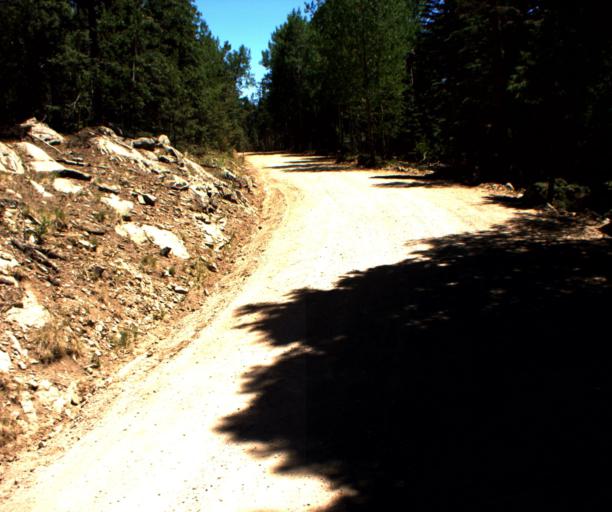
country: US
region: Arizona
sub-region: Graham County
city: Swift Trail Junction
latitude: 32.7006
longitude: -109.9104
